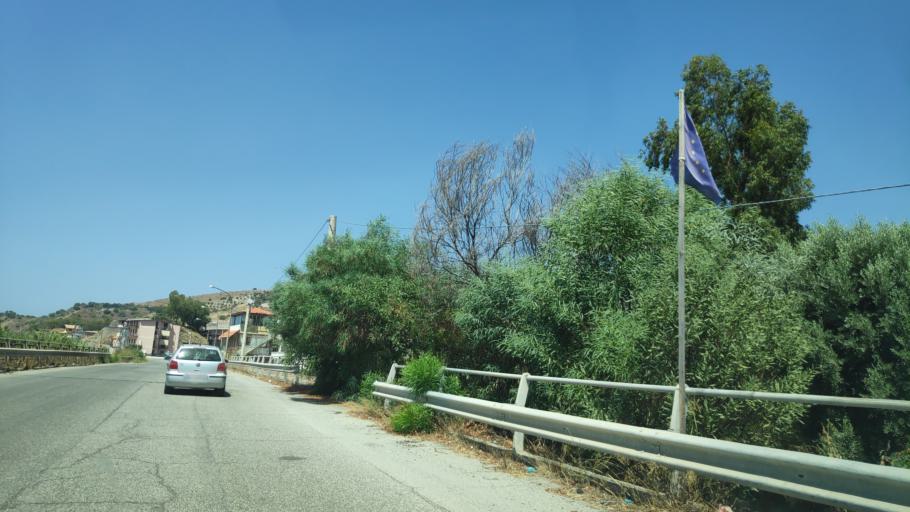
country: IT
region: Calabria
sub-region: Provincia di Reggio Calabria
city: Palizzi Marina
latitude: 37.9238
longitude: 15.9512
